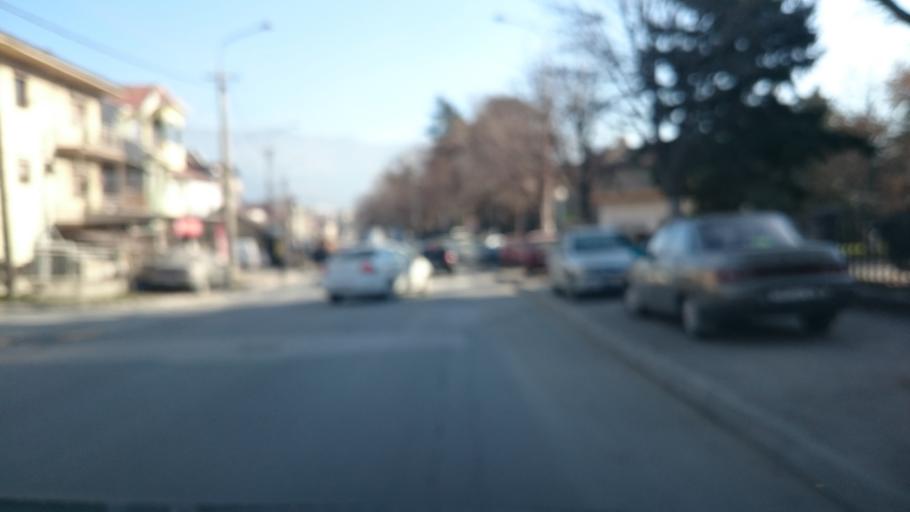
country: MK
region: Prilep
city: Prilep
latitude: 41.3510
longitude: 21.5474
